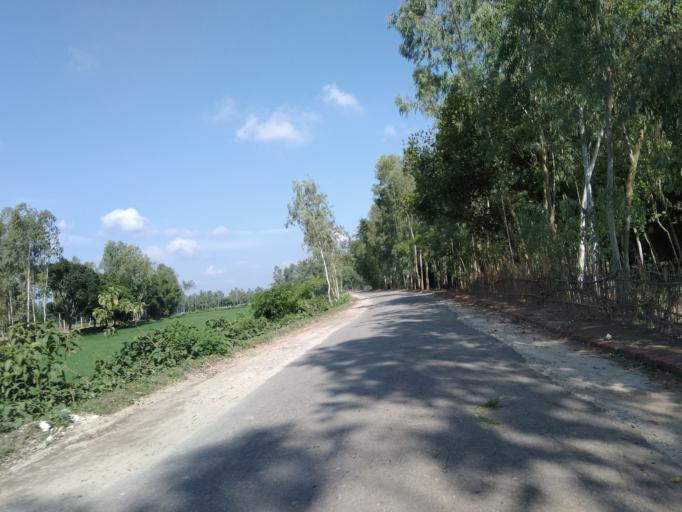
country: BD
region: Rangpur Division
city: Panchagarh
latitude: 26.2557
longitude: 88.6176
